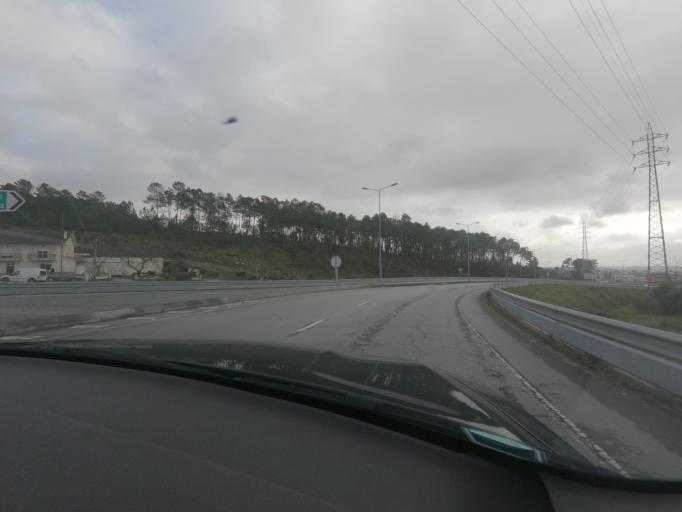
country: PT
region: Viseu
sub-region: Viseu
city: Abraveses
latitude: 40.6985
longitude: -7.9315
